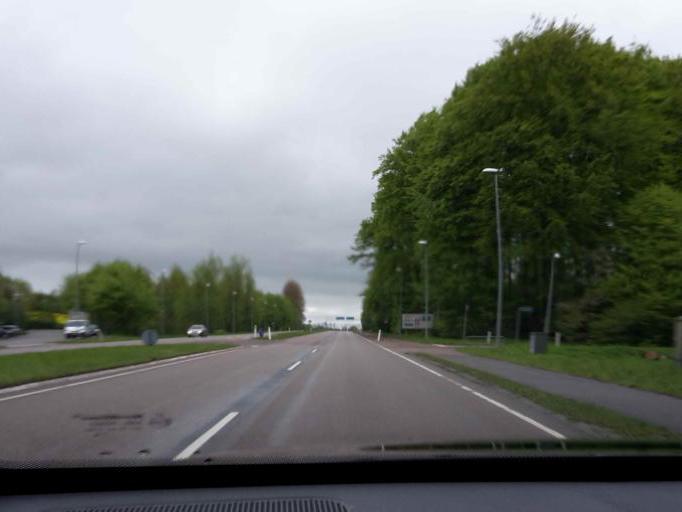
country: DK
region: South Denmark
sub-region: Assens Kommune
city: Tommerup Stationsby
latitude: 55.3887
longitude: 10.2236
